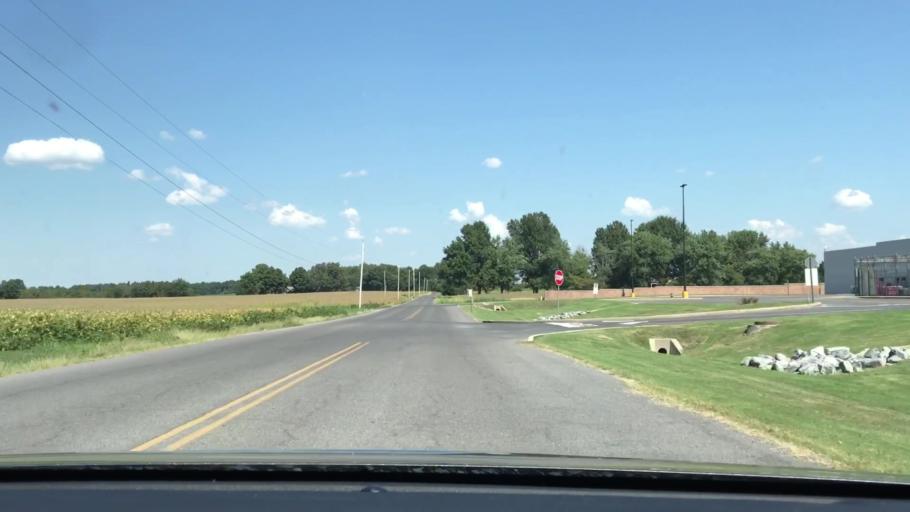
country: US
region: Kentucky
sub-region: Fulton County
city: Fulton
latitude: 36.5167
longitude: -88.9014
